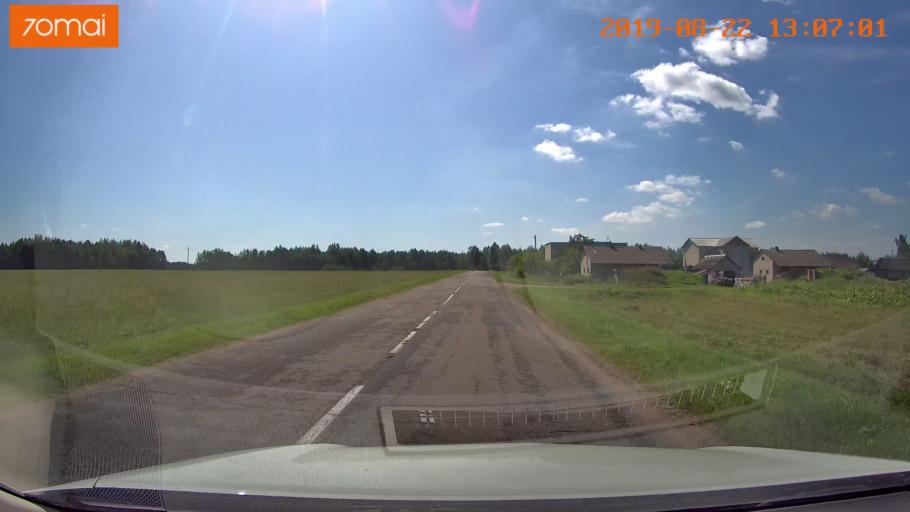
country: BY
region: Minsk
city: Prawdzinski
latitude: 53.3399
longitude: 27.8341
